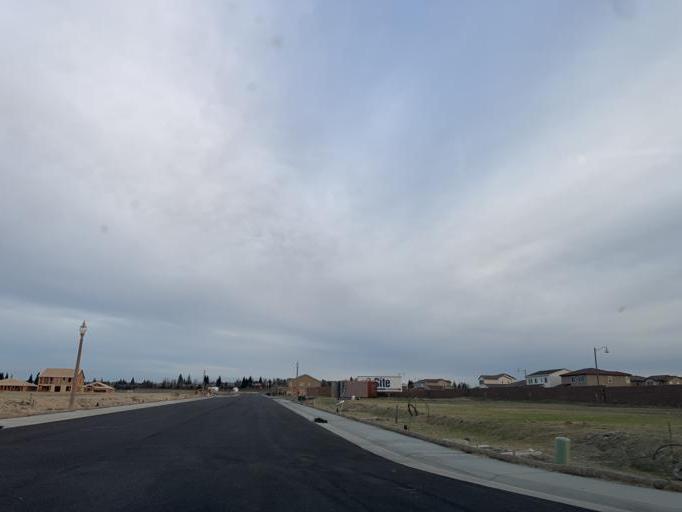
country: US
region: California
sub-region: Placer County
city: Lincoln
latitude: 38.8611
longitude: -121.2910
